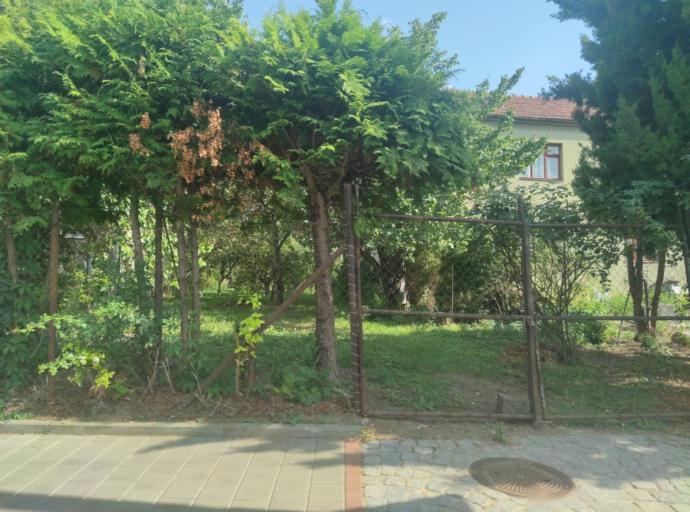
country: CZ
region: South Moravian
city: Podoli
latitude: 49.1745
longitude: 16.6849
